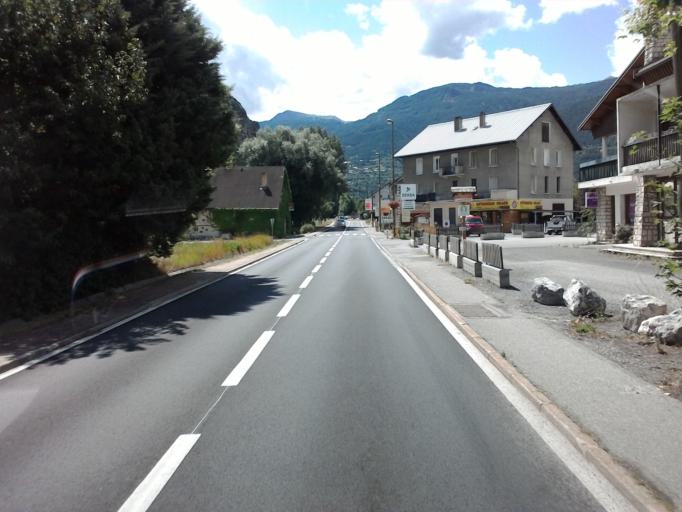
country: FR
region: Provence-Alpes-Cote d'Azur
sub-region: Departement des Hautes-Alpes
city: Guillestre
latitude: 44.6734
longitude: 6.6175
